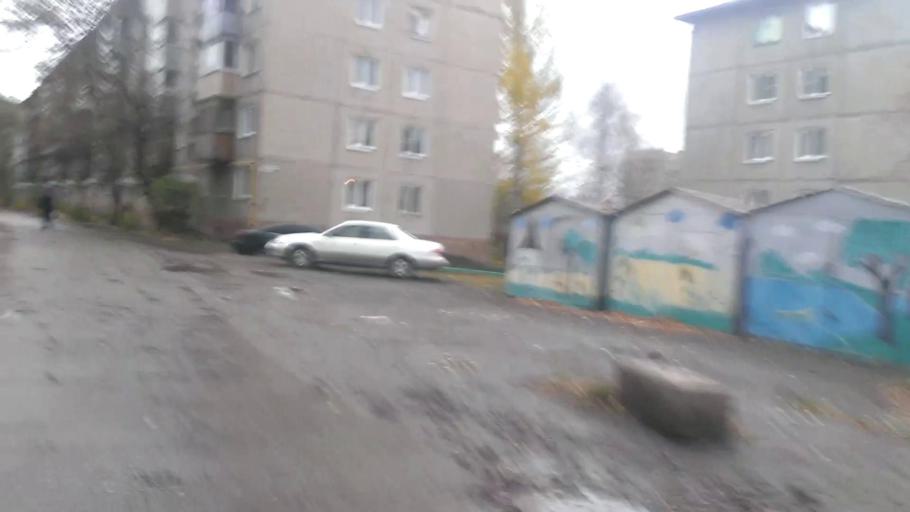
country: RU
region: Altai Krai
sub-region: Gorod Barnaulskiy
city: Barnaul
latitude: 53.3632
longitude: 83.6851
